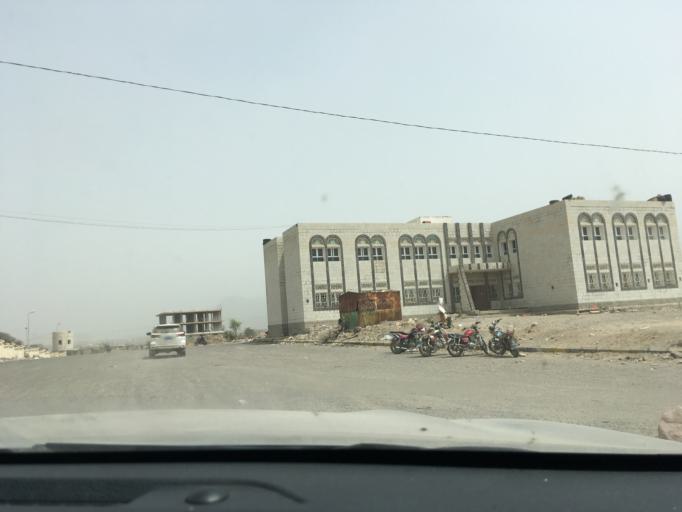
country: YE
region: Ad Dali'
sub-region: Qa'atabah
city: Qa`tabah
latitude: 13.8227
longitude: 44.7193
